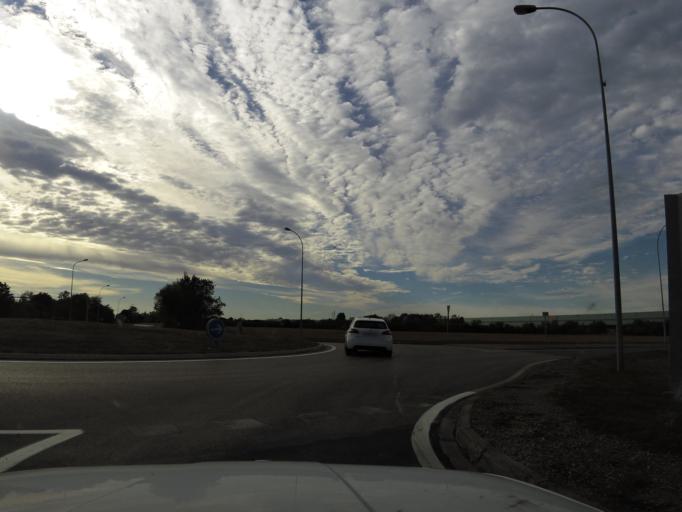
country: FR
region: Rhone-Alpes
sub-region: Departement de l'Isere
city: Hieres-sur-Amby
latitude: 45.8389
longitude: 5.2776
